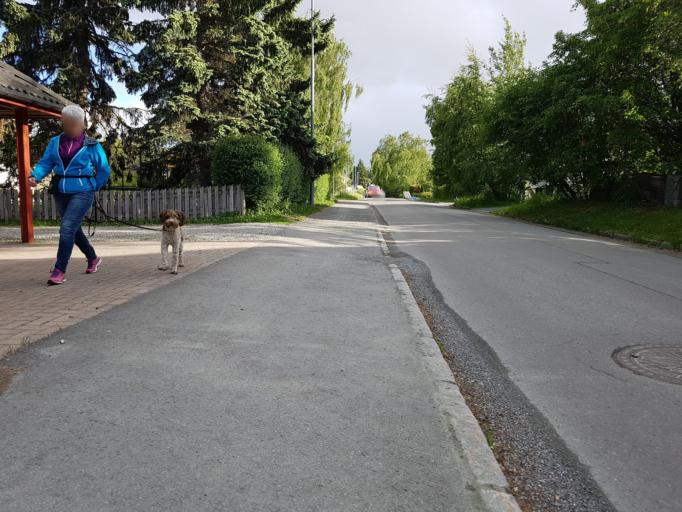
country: NO
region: Sor-Trondelag
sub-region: Trondheim
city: Trondheim
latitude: 63.4298
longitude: 10.4605
